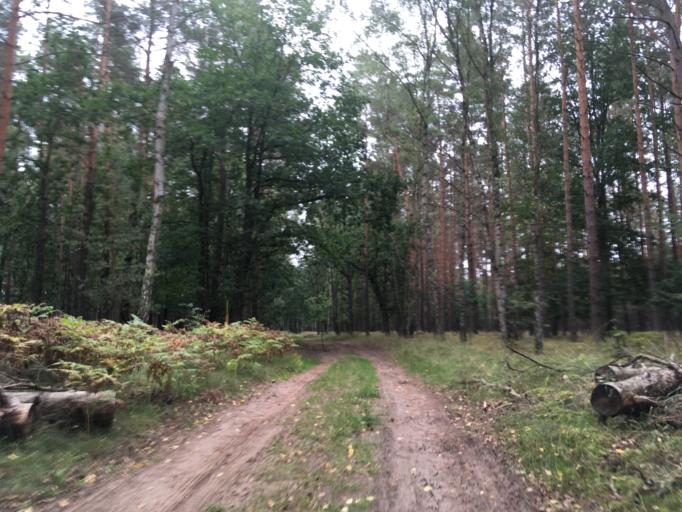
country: DE
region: Brandenburg
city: Zehdenick
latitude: 53.0388
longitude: 13.3393
